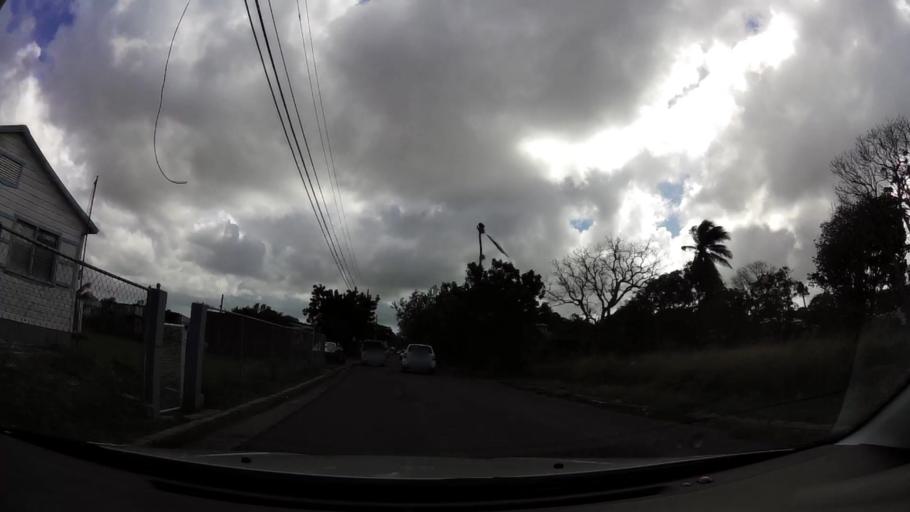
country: AG
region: Saint John
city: Saint John's
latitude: 17.1050
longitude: -61.8415
